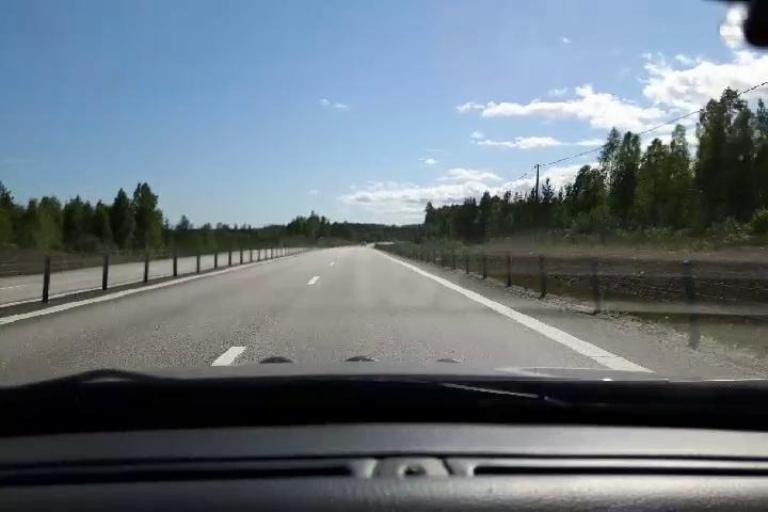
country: SE
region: Gaevleborg
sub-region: Hudiksvalls Kommun
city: Iggesund
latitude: 61.6734
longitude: 17.0325
